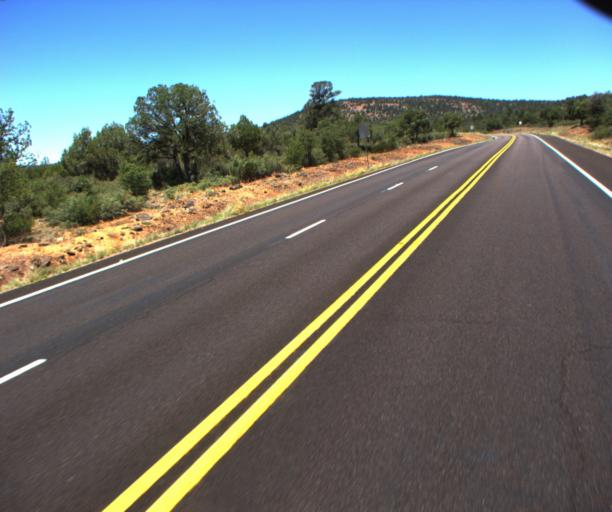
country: US
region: Arizona
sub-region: Gila County
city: Pine
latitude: 34.3375
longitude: -111.4216
